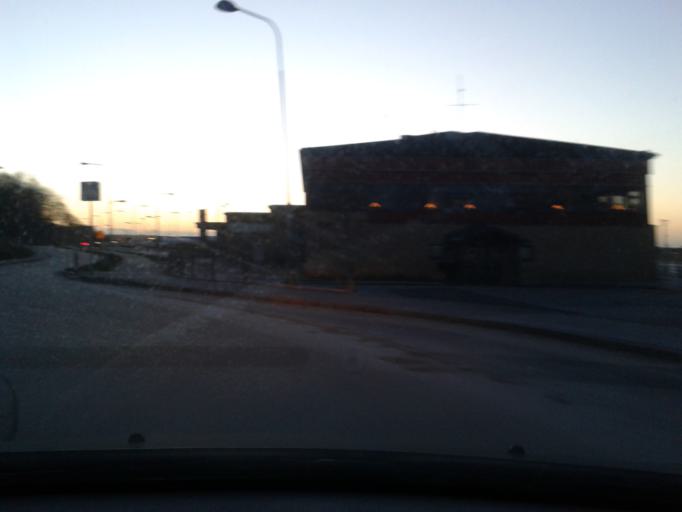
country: SE
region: Gotland
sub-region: Gotland
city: Visby
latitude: 57.6366
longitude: 18.2858
